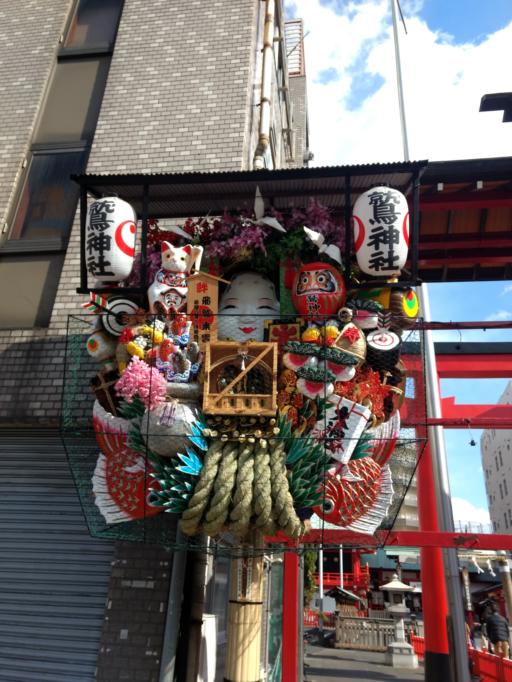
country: JP
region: Saitama
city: Soka
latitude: 35.7226
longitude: 139.7913
